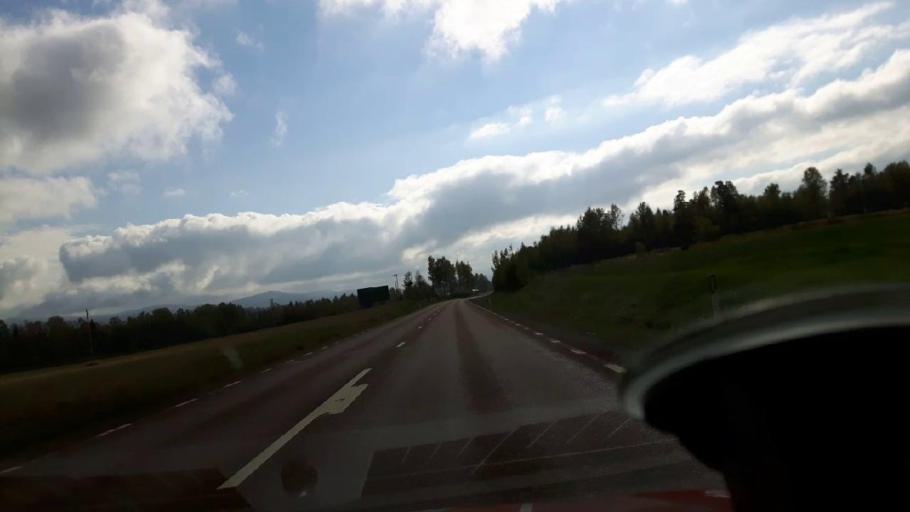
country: SE
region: Gaevleborg
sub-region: Bollnas Kommun
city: Arbra
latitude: 61.5384
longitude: 16.3603
